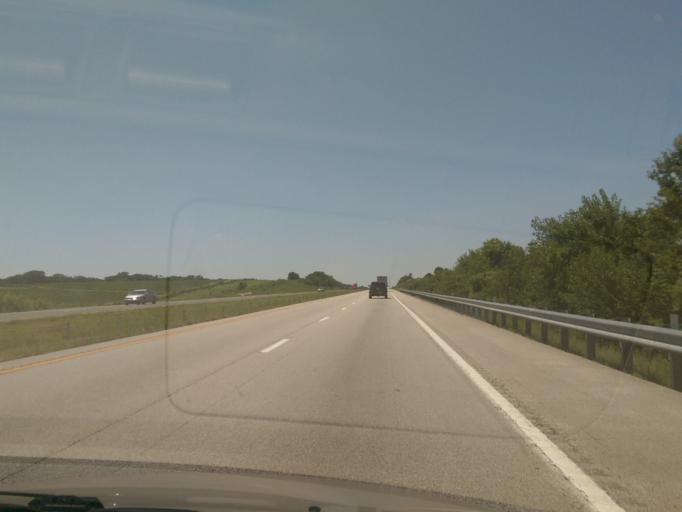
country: US
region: Missouri
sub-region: Cooper County
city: Boonville
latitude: 38.9345
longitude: -92.9247
